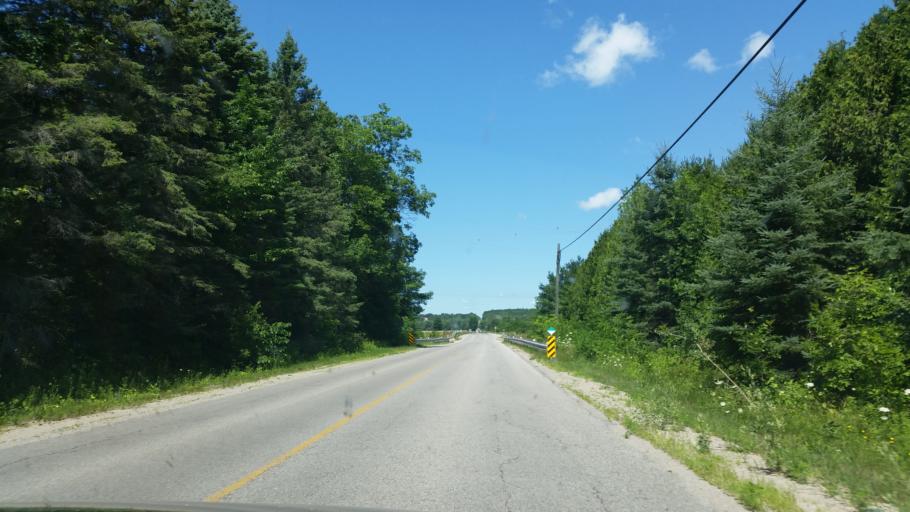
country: CA
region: Ontario
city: Barrie
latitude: 44.4525
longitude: -79.7871
